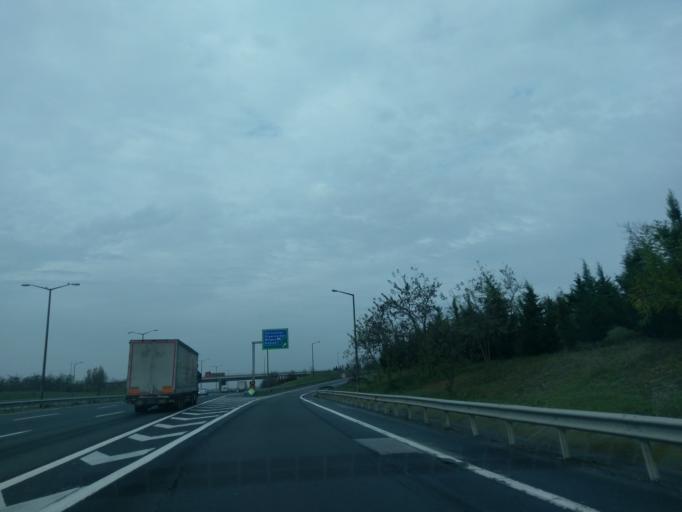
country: TR
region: Istanbul
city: Buyukcavuslu
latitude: 41.1922
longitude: 28.0875
